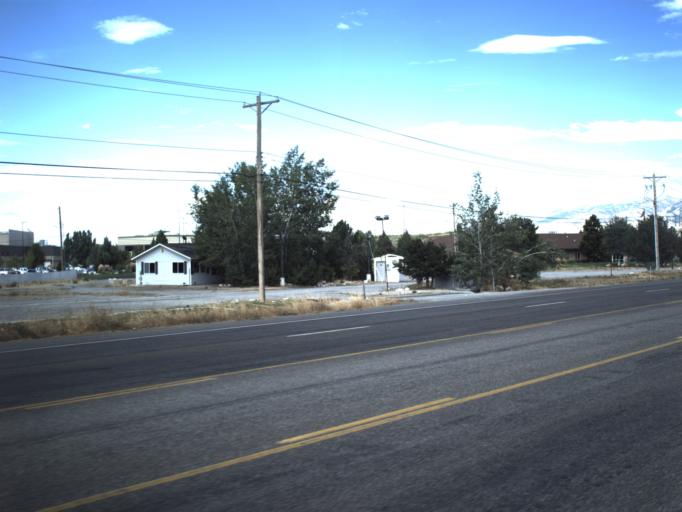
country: US
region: Utah
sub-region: Cache County
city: Nibley
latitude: 41.6988
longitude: -111.8578
